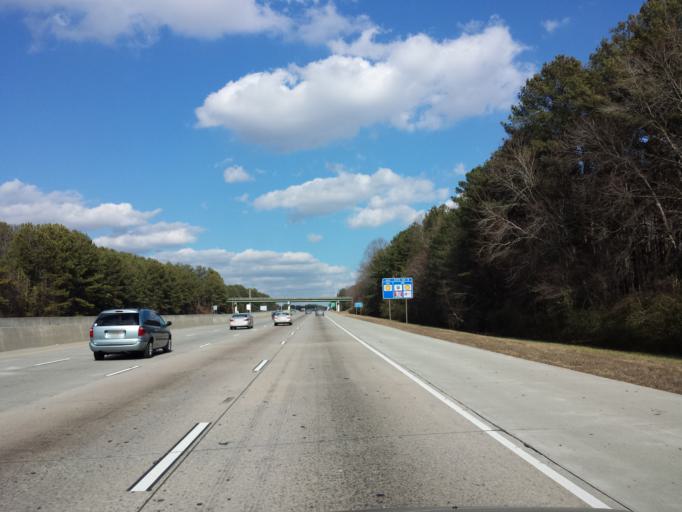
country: US
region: Georgia
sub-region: Fulton County
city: Alpharetta
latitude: 34.1006
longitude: -84.2471
